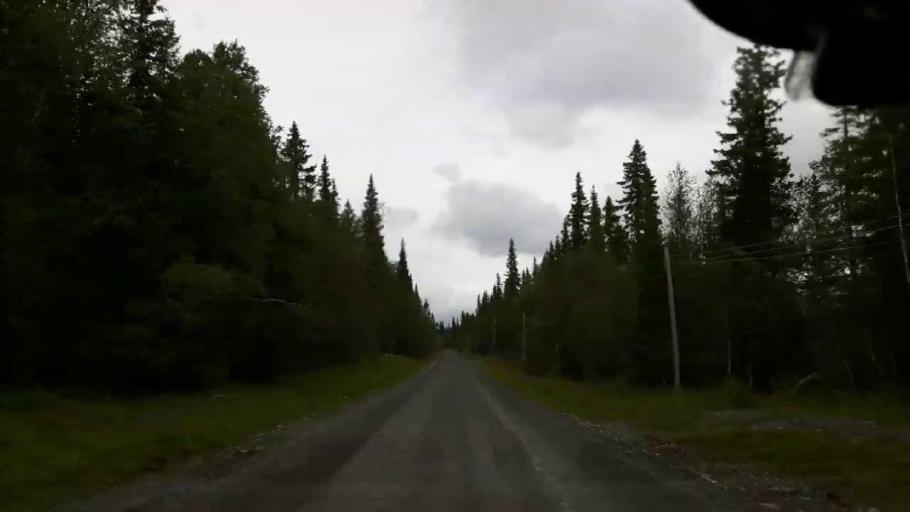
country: SE
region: Jaemtland
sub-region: Krokoms Kommun
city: Valla
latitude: 63.7136
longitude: 13.8606
